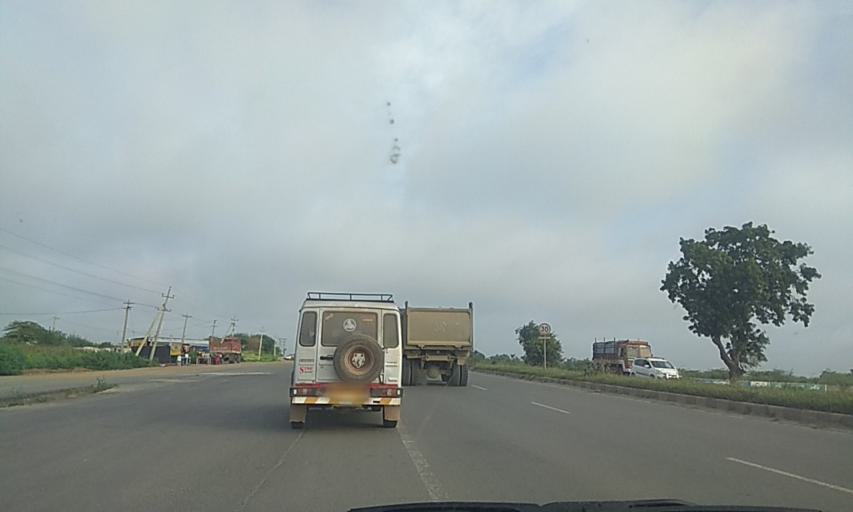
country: IN
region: Karnataka
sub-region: Haveri
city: Haveri
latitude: 14.7688
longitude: 75.4256
